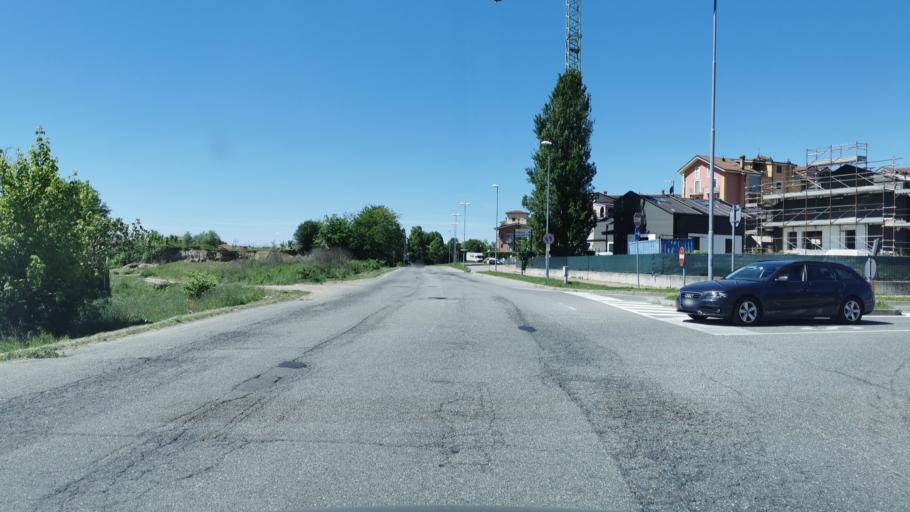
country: IT
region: Piedmont
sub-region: Provincia di Torino
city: Leini
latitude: 45.1806
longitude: 7.7210
